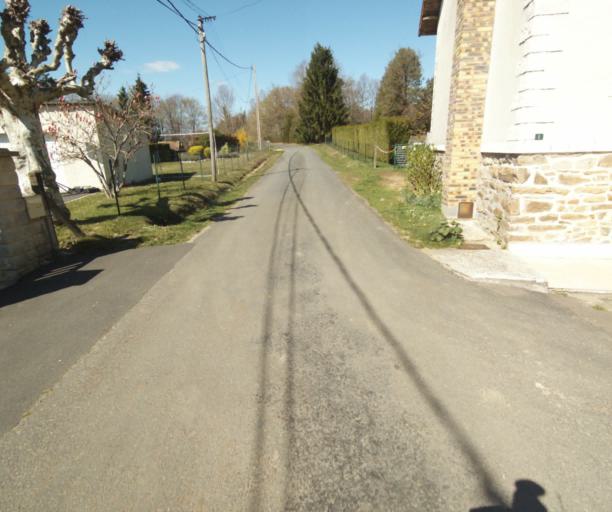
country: FR
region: Limousin
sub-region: Departement de la Correze
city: Saint-Clement
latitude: 45.3111
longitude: 1.6787
